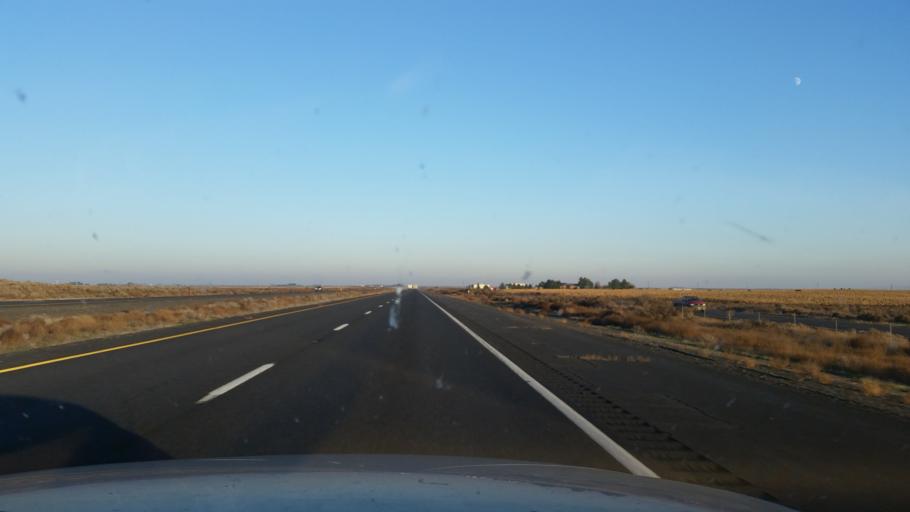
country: US
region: Washington
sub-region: Grant County
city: Royal City
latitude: 47.1036
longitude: -119.6732
